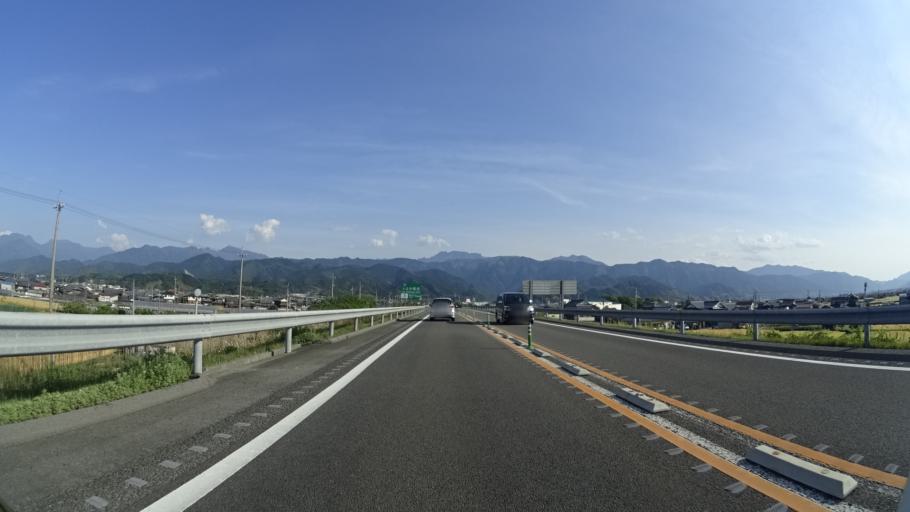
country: JP
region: Ehime
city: Saijo
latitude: 33.9033
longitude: 133.0756
